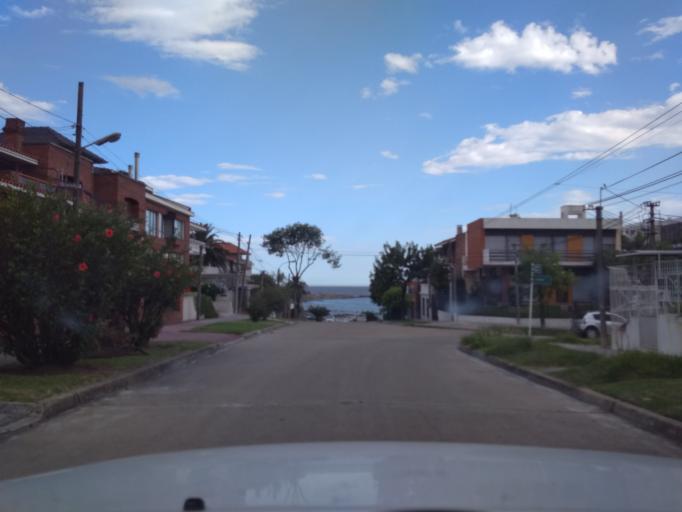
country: UY
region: Canelones
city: Paso de Carrasco
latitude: -34.8941
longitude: -56.0870
